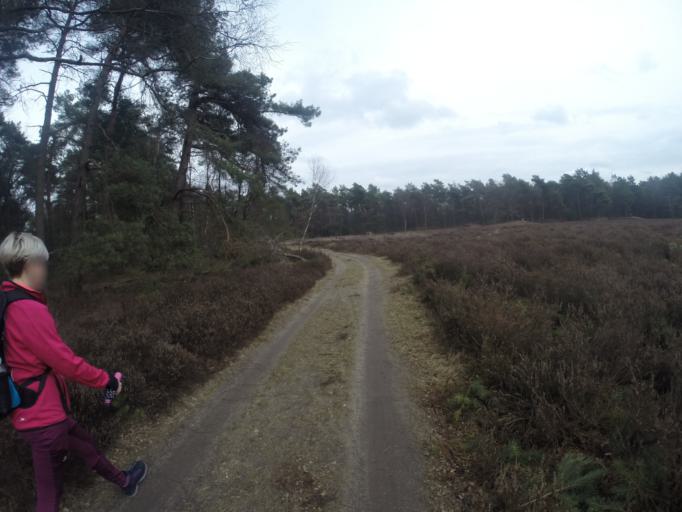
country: NL
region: Gelderland
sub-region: Gemeente Bronckhorst
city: Zelhem
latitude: 52.0436
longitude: 6.3860
